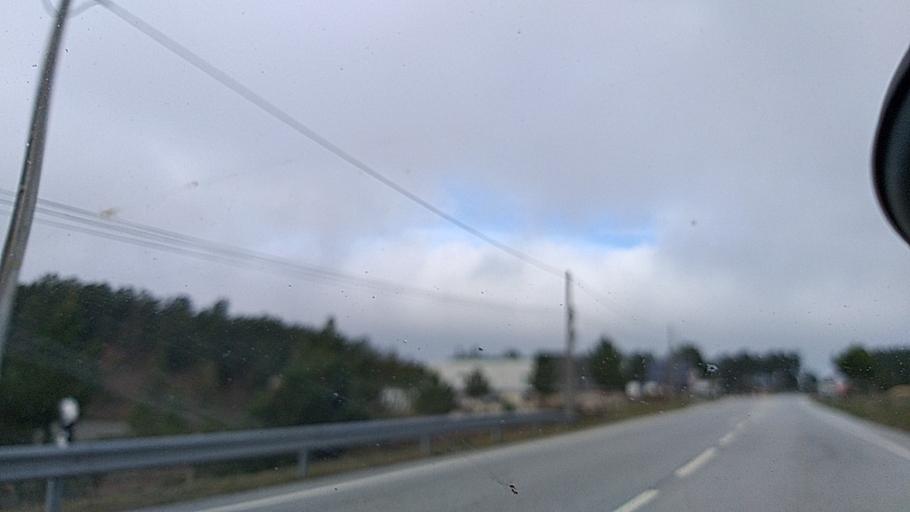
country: PT
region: Guarda
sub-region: Aguiar da Beira
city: Aguiar da Beira
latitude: 40.7874
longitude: -7.5027
